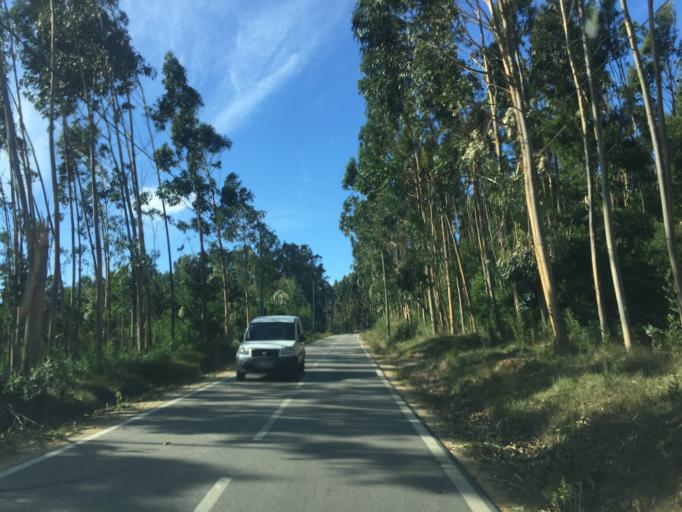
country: PT
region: Coimbra
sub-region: Figueira da Foz
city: Buarcos
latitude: 40.1915
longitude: -8.8781
